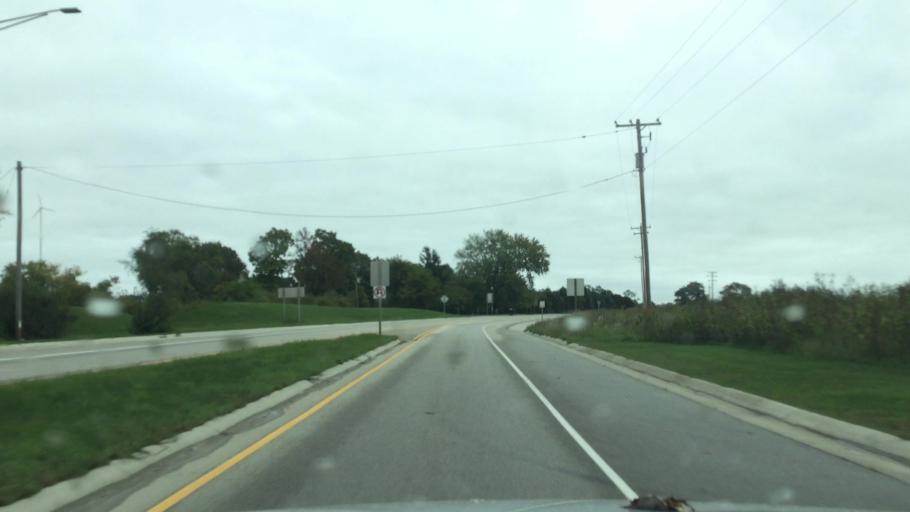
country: US
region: Wisconsin
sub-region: Racine County
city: Eagle Lake
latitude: 42.7420
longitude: -88.1095
